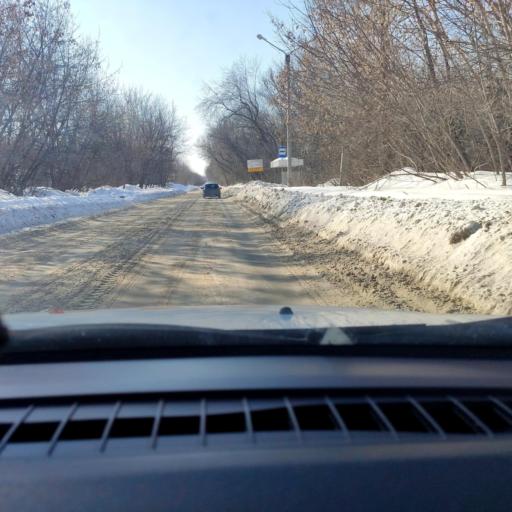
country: RU
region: Samara
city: Novokuybyshevsk
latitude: 53.1187
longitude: 49.9106
